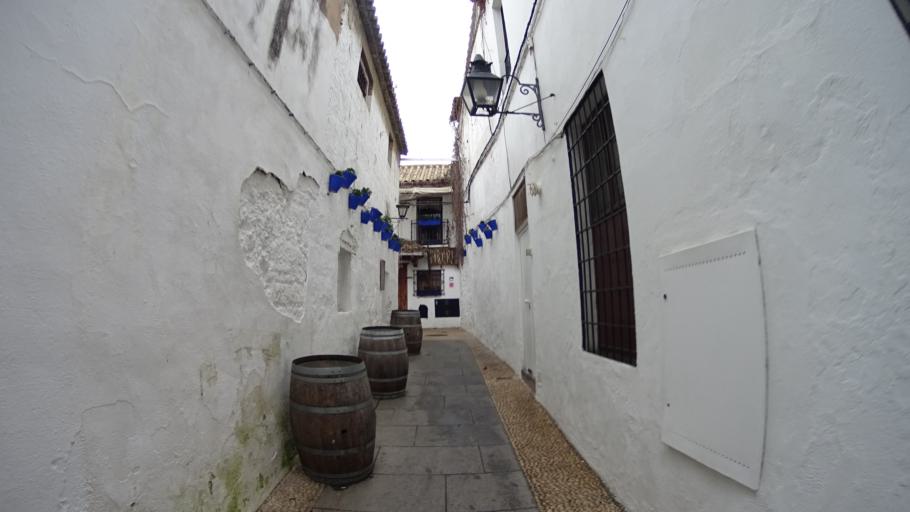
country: ES
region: Andalusia
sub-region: Province of Cordoba
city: Cordoba
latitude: 37.8782
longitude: -4.7819
